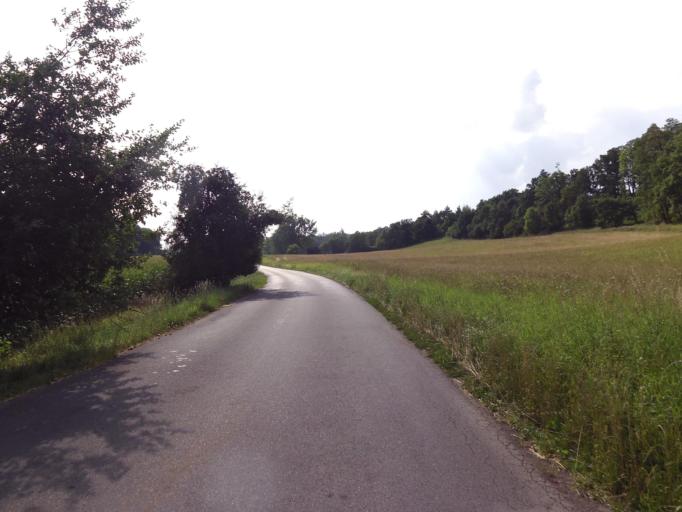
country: CZ
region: Central Bohemia
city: Mnichovo Hradiste
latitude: 50.5703
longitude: 15.0056
